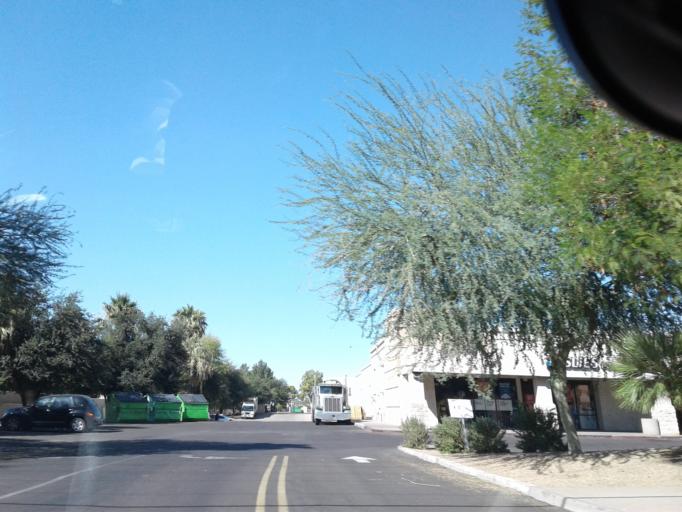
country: US
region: Arizona
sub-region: Maricopa County
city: Scottsdale
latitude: 33.4789
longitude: -111.9091
